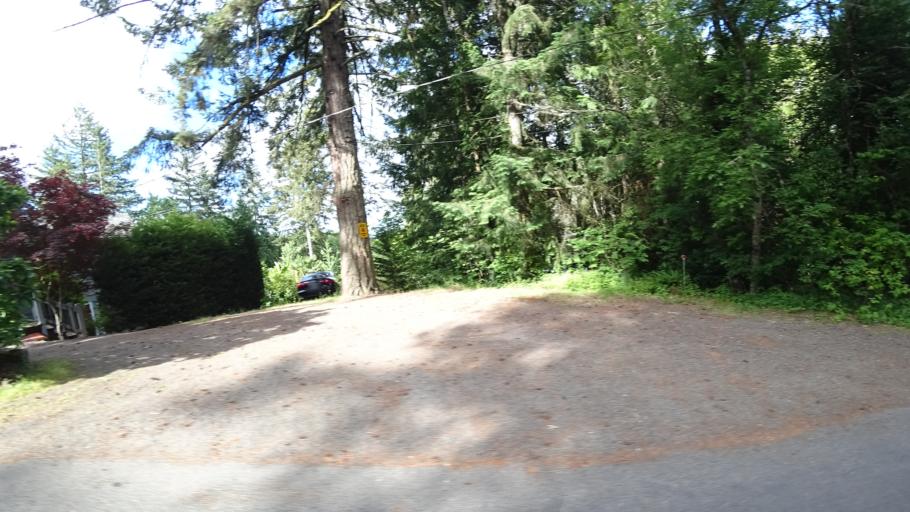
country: US
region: Oregon
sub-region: Washington County
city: Oak Hills
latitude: 45.5796
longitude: -122.8165
